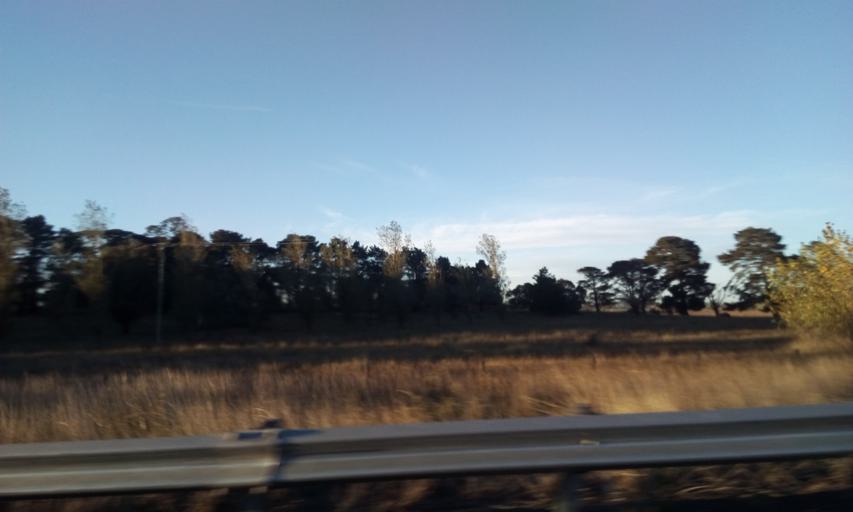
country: AU
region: New South Wales
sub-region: Goulburn Mulwaree
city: Goulburn
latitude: -34.8931
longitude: 149.5179
